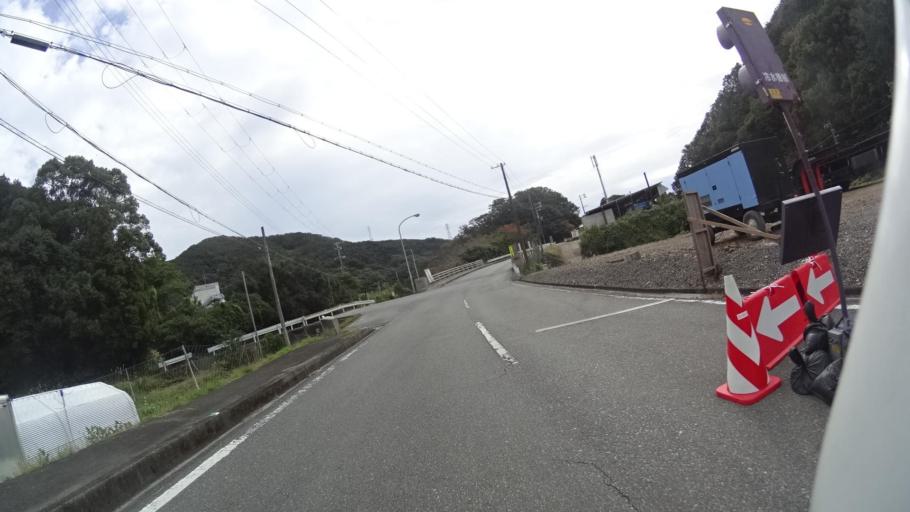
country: JP
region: Wakayama
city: Shingu
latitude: 33.4931
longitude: 135.7607
